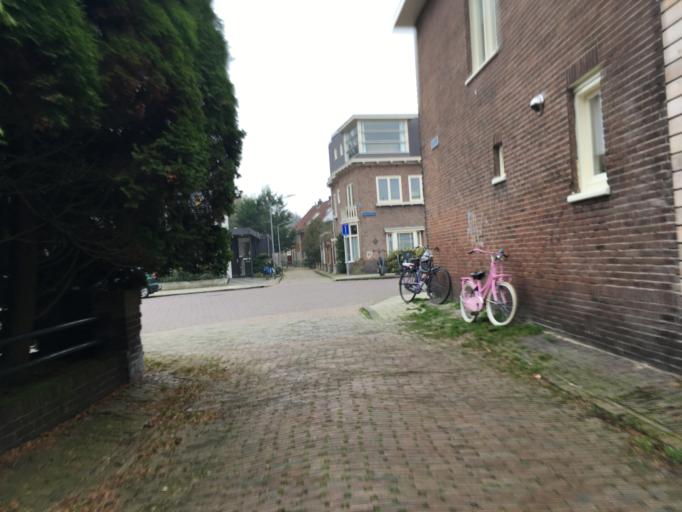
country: NL
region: North Holland
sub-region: Gemeente Haarlem
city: Haarlem
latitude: 52.3986
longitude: 4.6404
